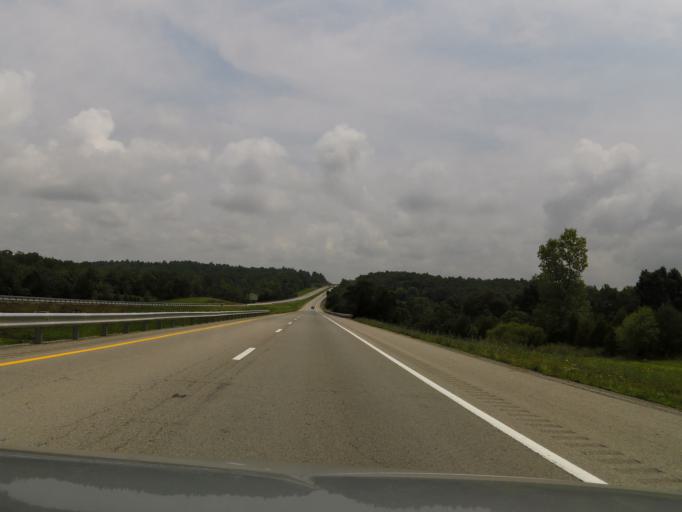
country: US
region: Kentucky
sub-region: Grayson County
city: Leitchfield
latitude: 37.4699
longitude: -86.2618
